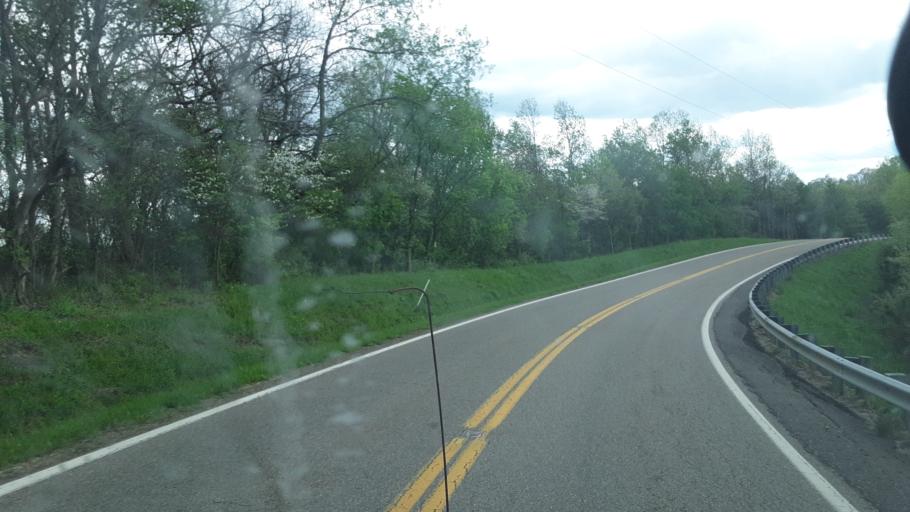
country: US
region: Ohio
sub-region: Noble County
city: Caldwell
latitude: 39.7437
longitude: -81.6361
